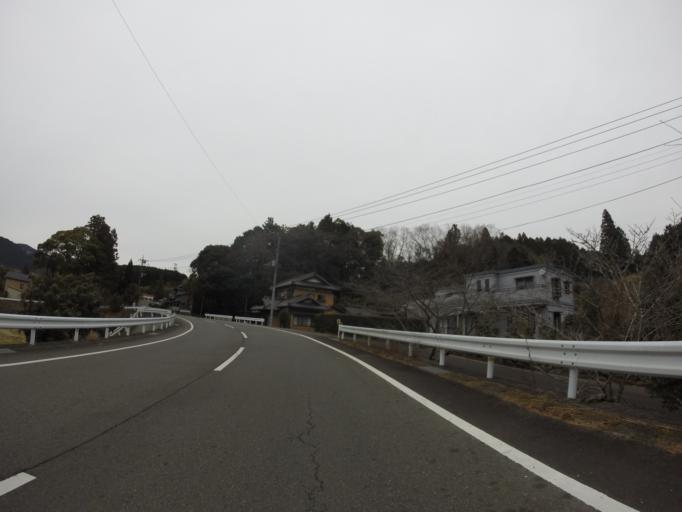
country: JP
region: Shizuoka
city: Fujinomiya
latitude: 35.2448
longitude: 138.5702
